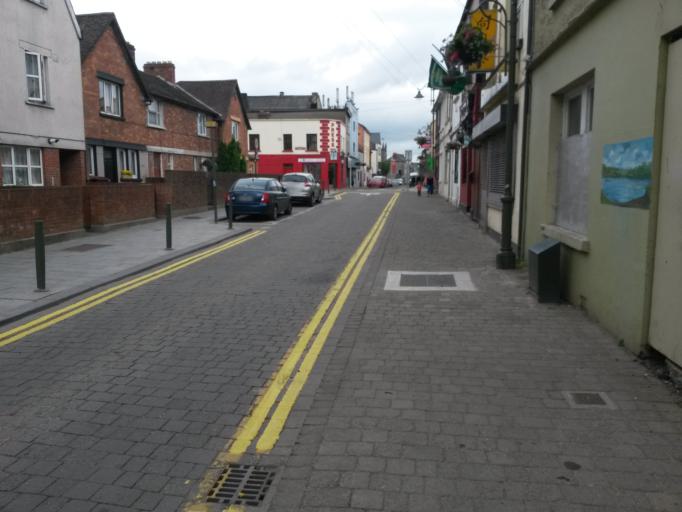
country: IE
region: Munster
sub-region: County Limerick
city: Luimneach
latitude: 52.6687
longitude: -8.6234
